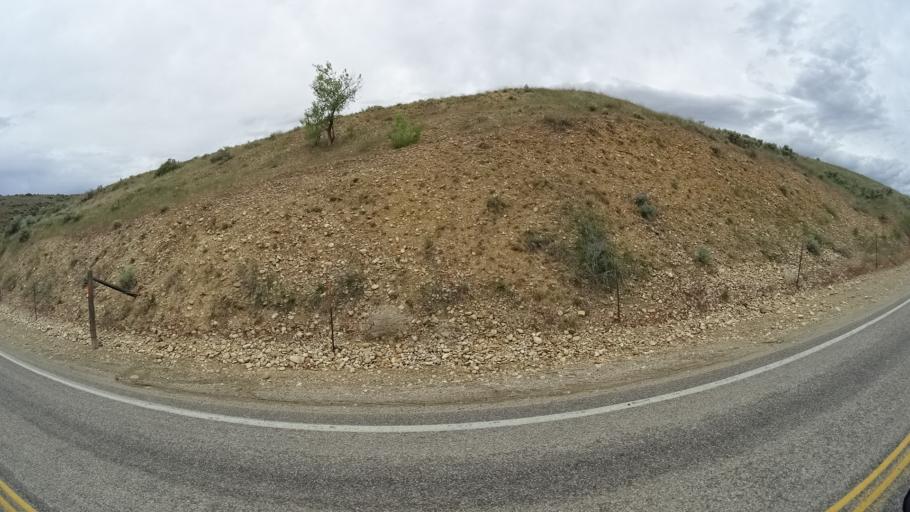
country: US
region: Idaho
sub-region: Ada County
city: Boise
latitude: 43.4799
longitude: -116.0215
